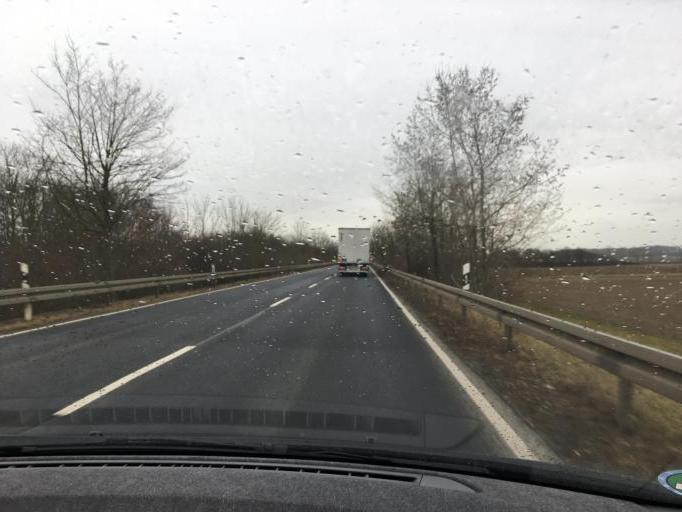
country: DE
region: North Rhine-Westphalia
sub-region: Regierungsbezirk Koln
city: Bergheim
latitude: 50.9281
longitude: 6.6138
